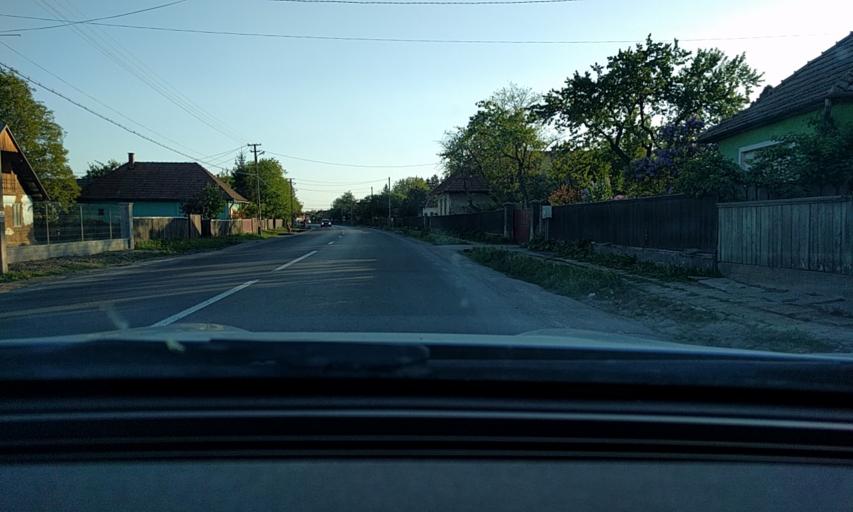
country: RO
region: Covasna
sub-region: Municipiul Targu Secuiesc
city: Lunga
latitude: 46.0252
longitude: 26.2232
